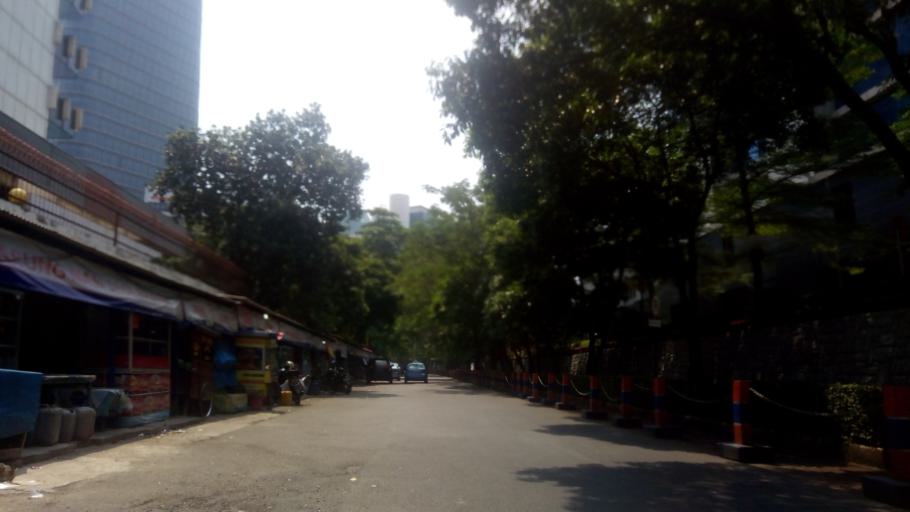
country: ID
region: Jakarta Raya
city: Jakarta
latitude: -6.2373
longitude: 106.8288
